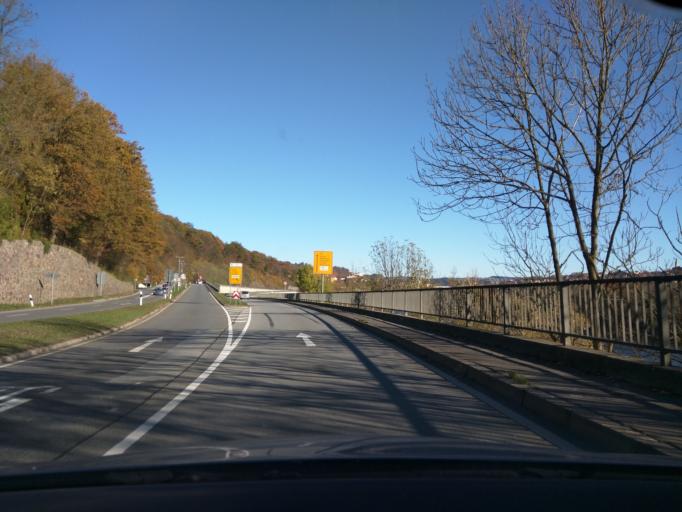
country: DE
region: Bavaria
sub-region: Lower Bavaria
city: Passau
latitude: 48.5754
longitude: 13.4229
